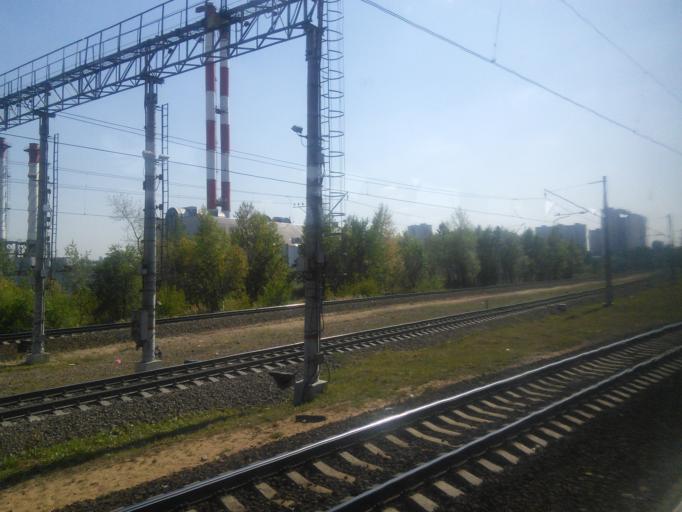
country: RU
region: Moskovskaya
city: Kur'yanovo
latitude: 55.6481
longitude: 37.6989
